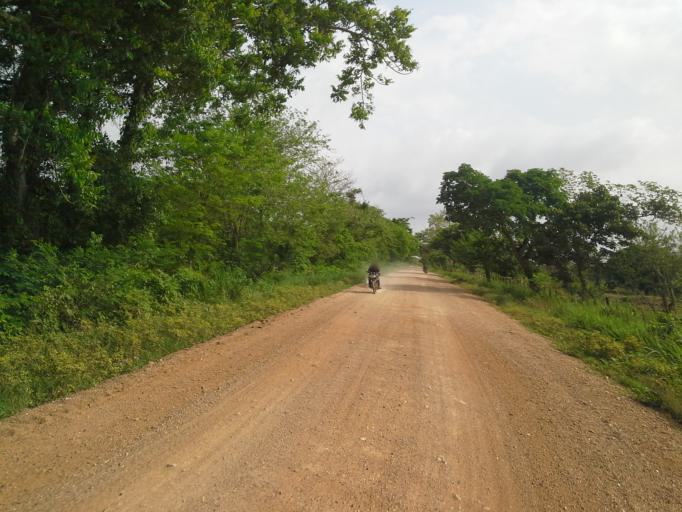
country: CO
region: Cordoba
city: Chima
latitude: 9.1276
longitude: -75.6093
